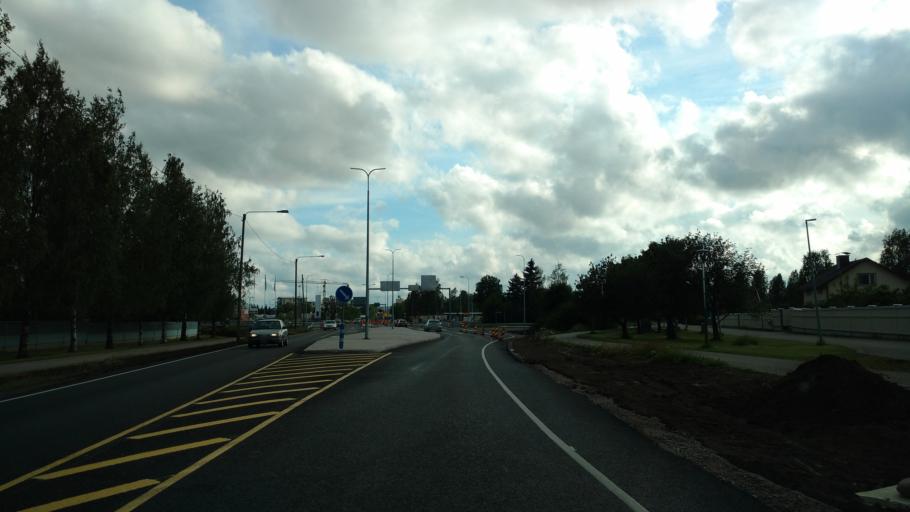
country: FI
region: Varsinais-Suomi
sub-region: Salo
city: Salo
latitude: 60.3951
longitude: 23.1338
